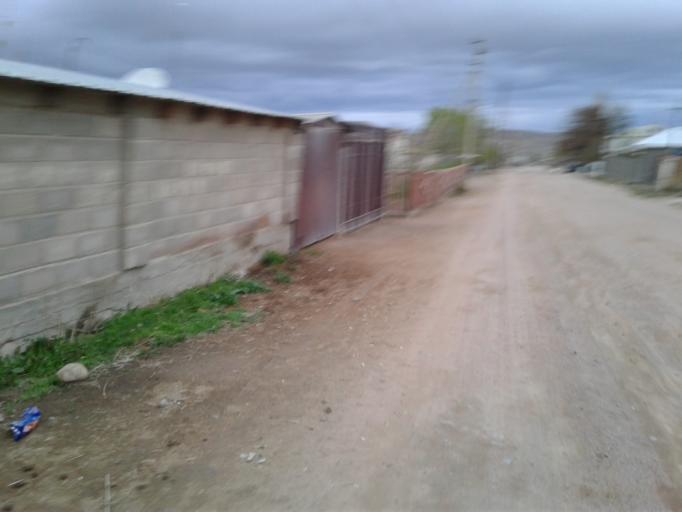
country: KG
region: Ysyk-Koel
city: Bokombayevskoye
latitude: 42.1170
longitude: 76.9878
